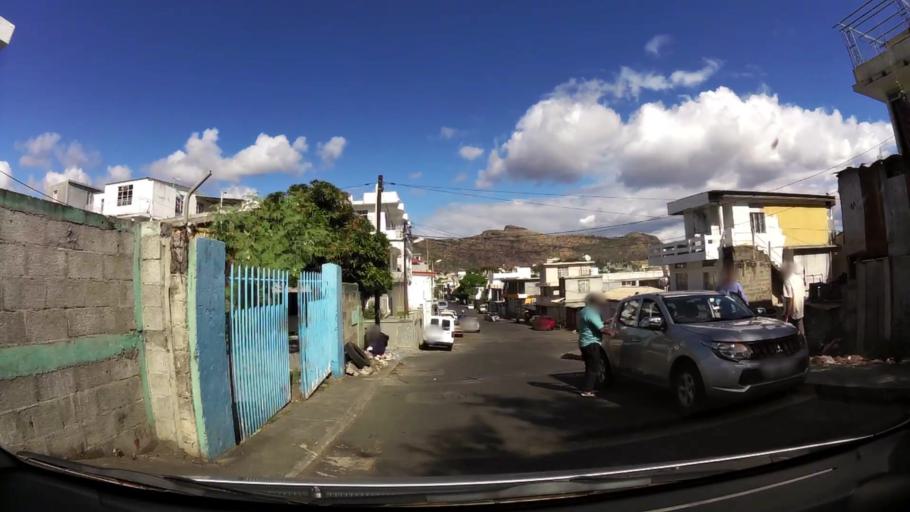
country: MU
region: Port Louis
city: Port Louis
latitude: -20.1643
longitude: 57.5192
